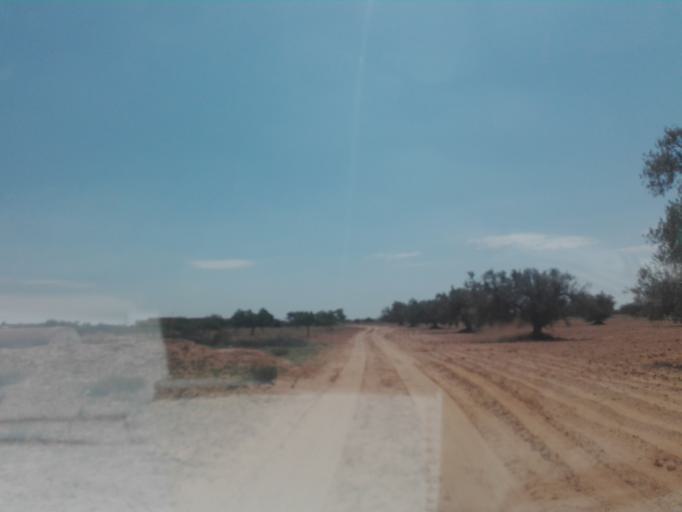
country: TN
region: Safaqis
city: Bi'r `Ali Bin Khalifah
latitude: 34.6128
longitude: 10.3504
